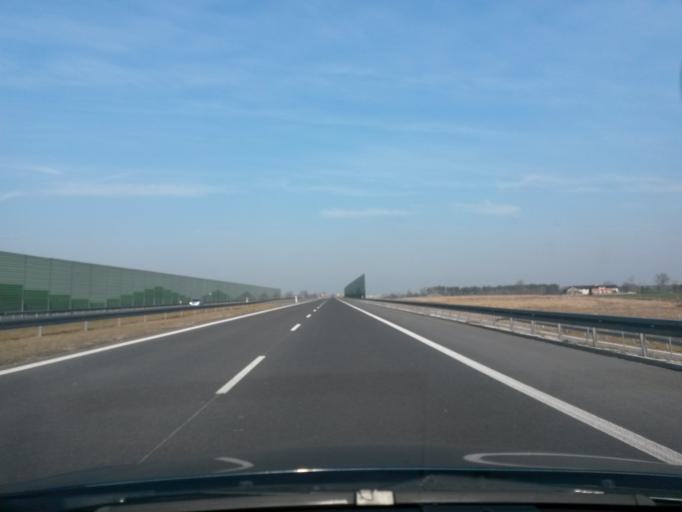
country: PL
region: Lodz Voivodeship
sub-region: Powiat leczycki
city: Piatek
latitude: 52.0895
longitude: 19.5219
